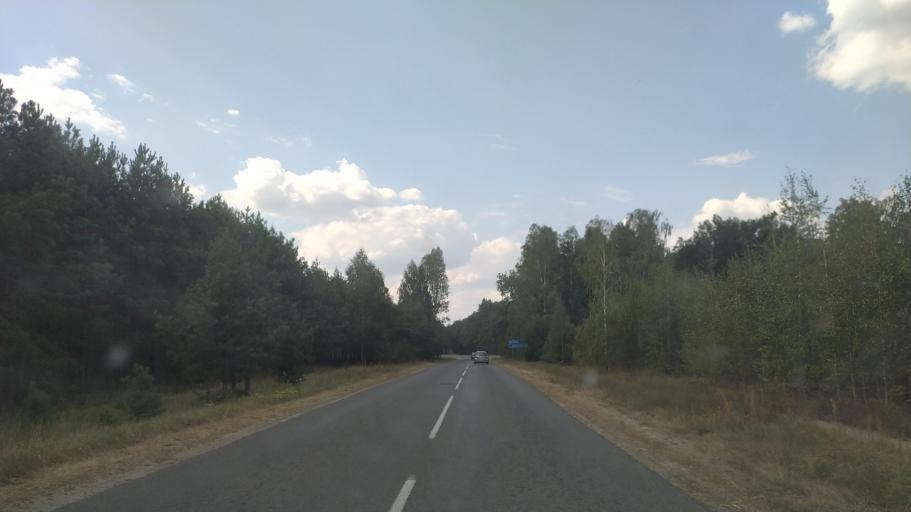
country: BY
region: Brest
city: Drahichyn
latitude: 52.1063
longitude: 25.1170
